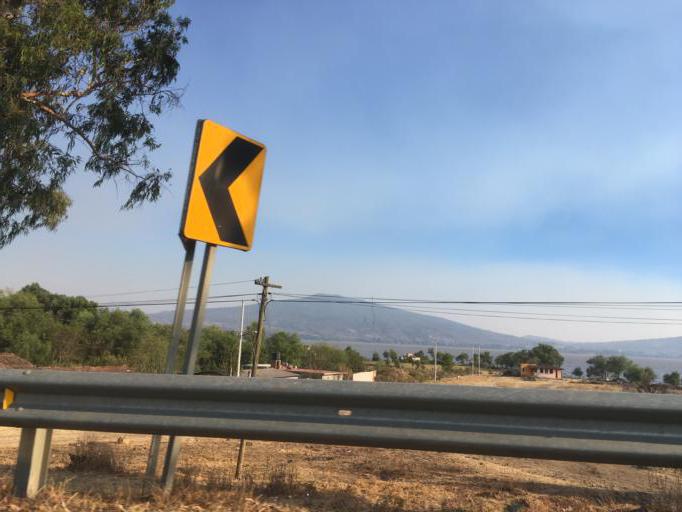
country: MX
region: Michoacan
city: Santa Fe de la Laguna
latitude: 19.6712
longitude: -101.5615
